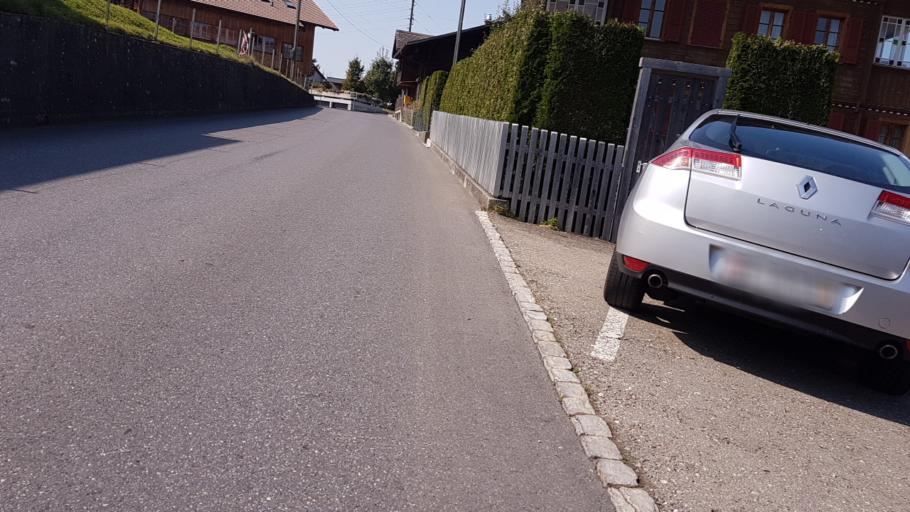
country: CH
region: Bern
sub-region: Frutigen-Niedersimmental District
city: Aeschi
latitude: 46.6505
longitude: 7.7114
